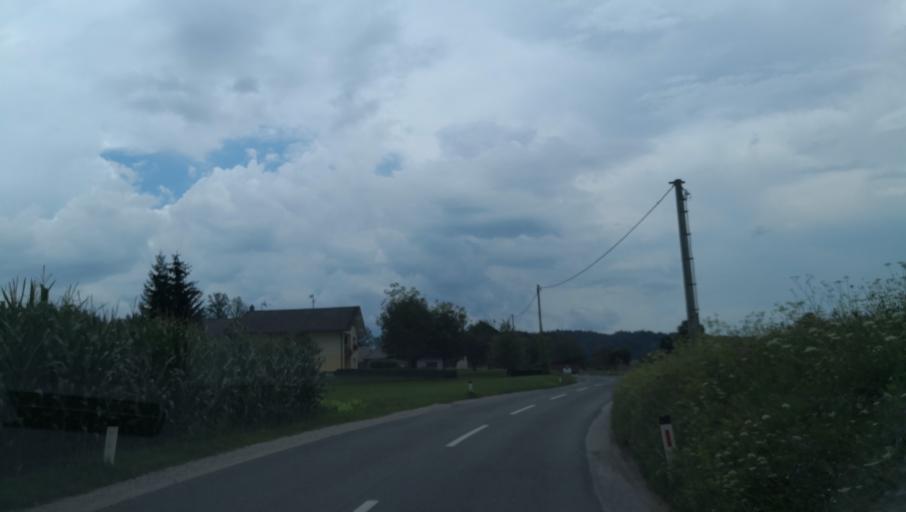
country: SI
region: Ivancna Gorica
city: Ivancna Gorica
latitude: 45.8702
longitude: 14.8216
